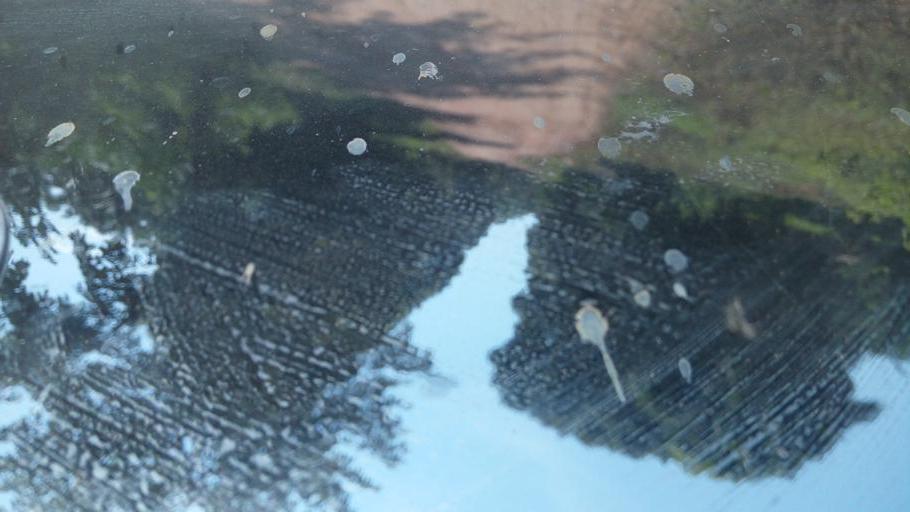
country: CD
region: South Kivu
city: Uvira
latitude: -3.7052
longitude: 29.1231
